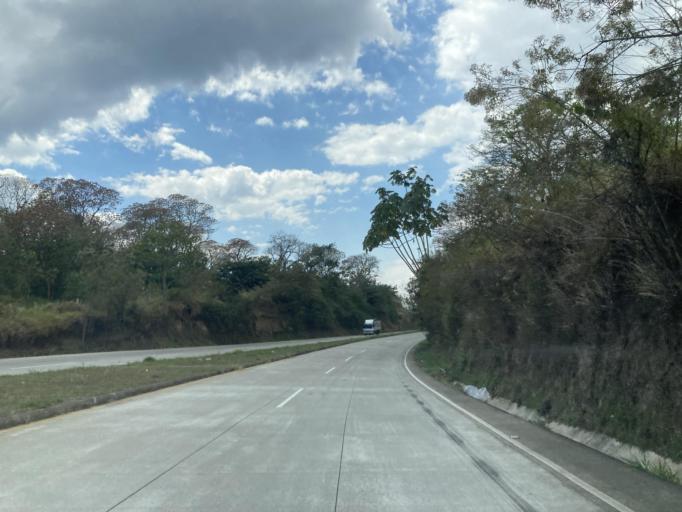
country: GT
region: Santa Rosa
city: Barberena
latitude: 14.3136
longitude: -90.3969
